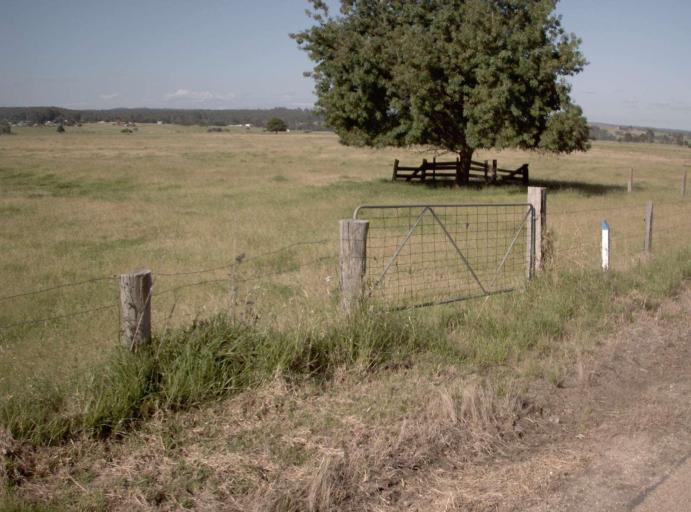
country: AU
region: Victoria
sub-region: East Gippsland
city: Lakes Entrance
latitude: -37.7186
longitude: 148.4667
